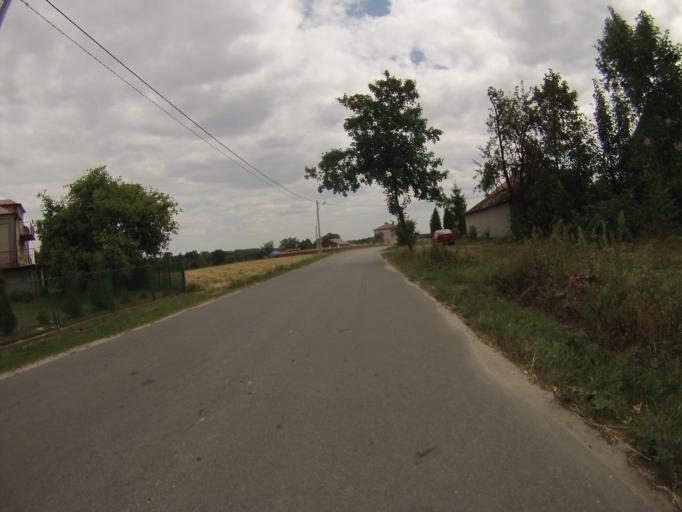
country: PL
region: Swietokrzyskie
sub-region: Powiat staszowski
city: Bogoria
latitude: 50.6855
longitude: 21.2154
